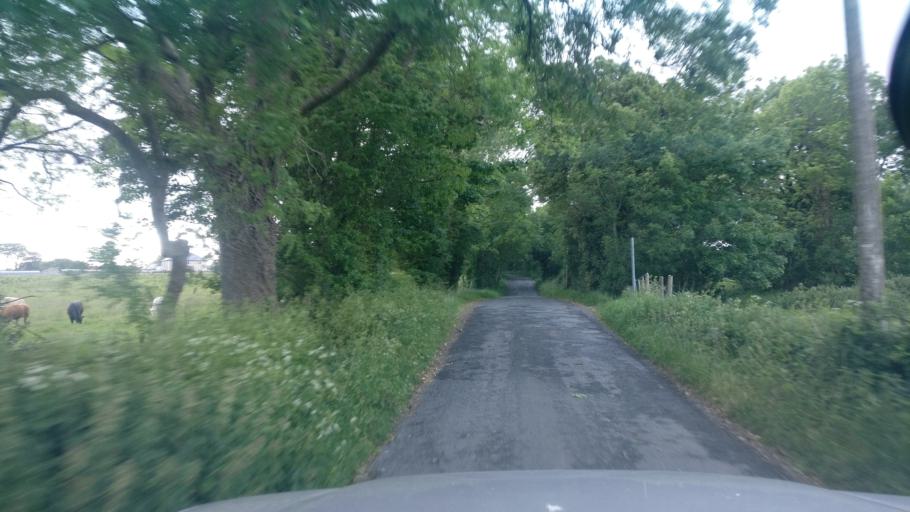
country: IE
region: Connaught
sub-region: County Galway
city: Ballinasloe
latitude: 53.2330
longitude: -8.1954
